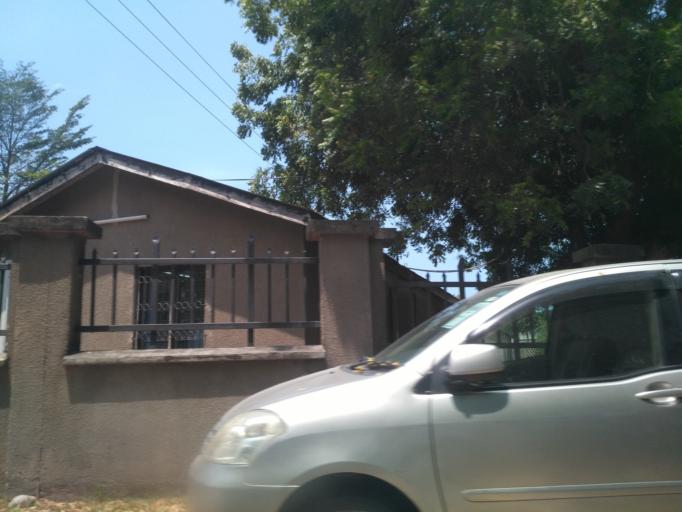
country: TZ
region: Dar es Salaam
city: Dar es Salaam
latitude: -6.8063
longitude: 39.2727
